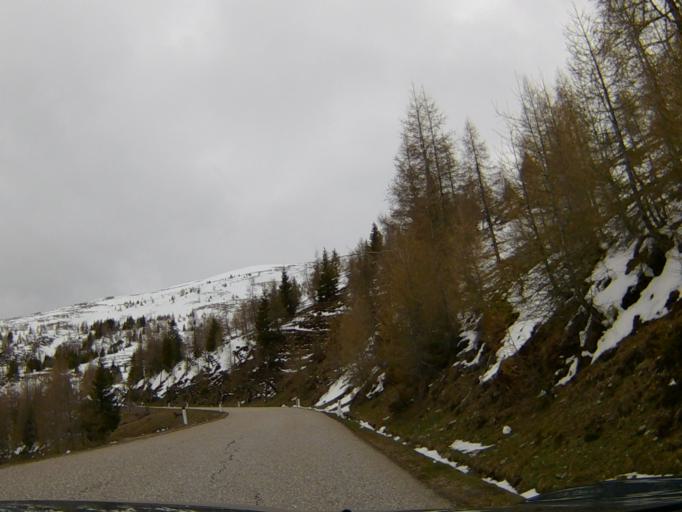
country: AT
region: Carinthia
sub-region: Politischer Bezirk Spittal an der Drau
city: Baldramsdorf
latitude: 46.7531
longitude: 13.4739
